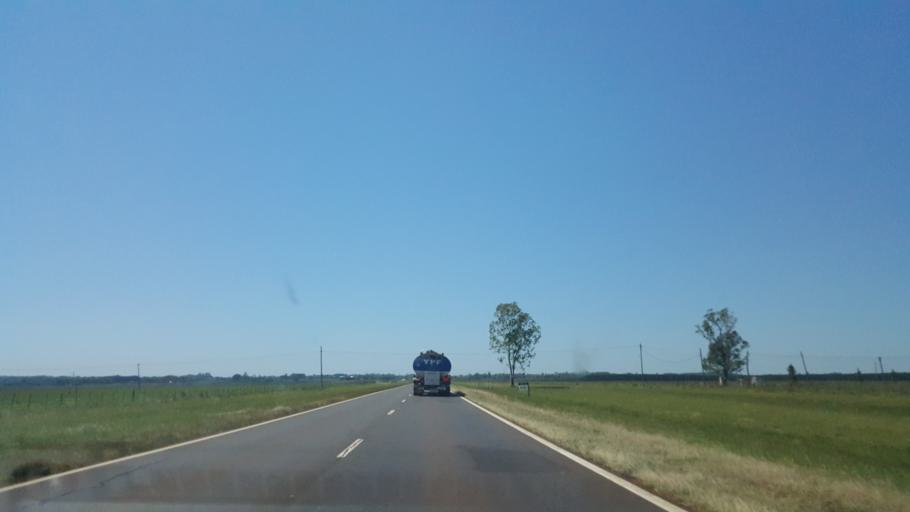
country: AR
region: Corrientes
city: Santo Tome
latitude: -28.5234
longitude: -56.1053
